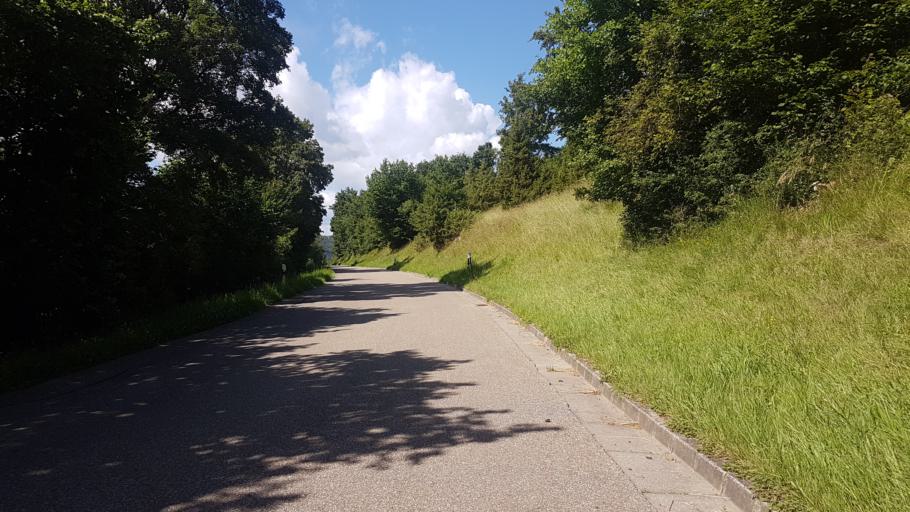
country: DE
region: Bavaria
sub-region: Upper Bavaria
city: Walting
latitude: 48.8921
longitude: 11.2618
